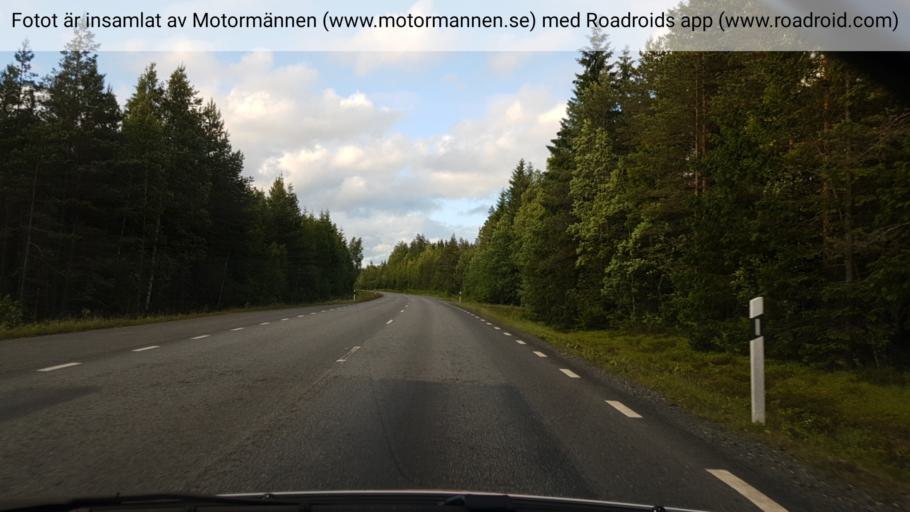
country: SE
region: OErebro
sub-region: Karlskoga Kommun
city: Karlskoga
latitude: 59.4255
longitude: 14.7087
